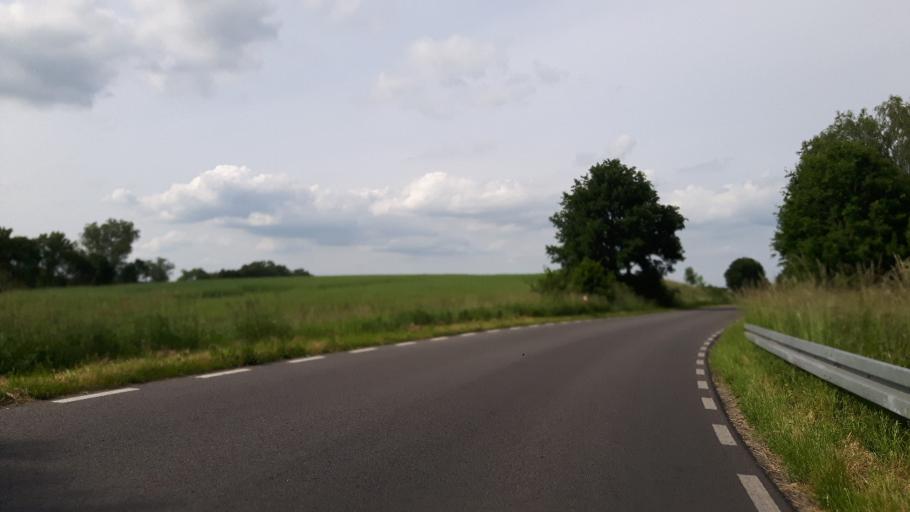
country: PL
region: West Pomeranian Voivodeship
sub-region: Powiat goleniowski
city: Nowogard
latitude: 53.7144
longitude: 15.1186
